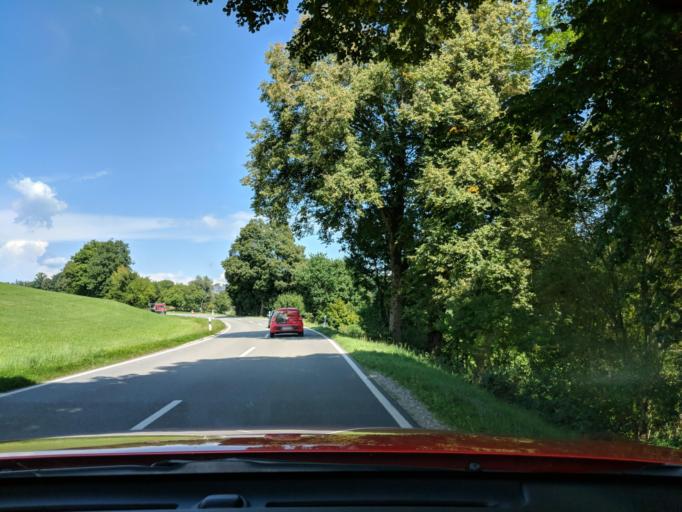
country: DE
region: Baden-Wuerttemberg
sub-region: Tuebingen Region
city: Wangen im Allgau
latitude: 47.7160
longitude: 9.8209
